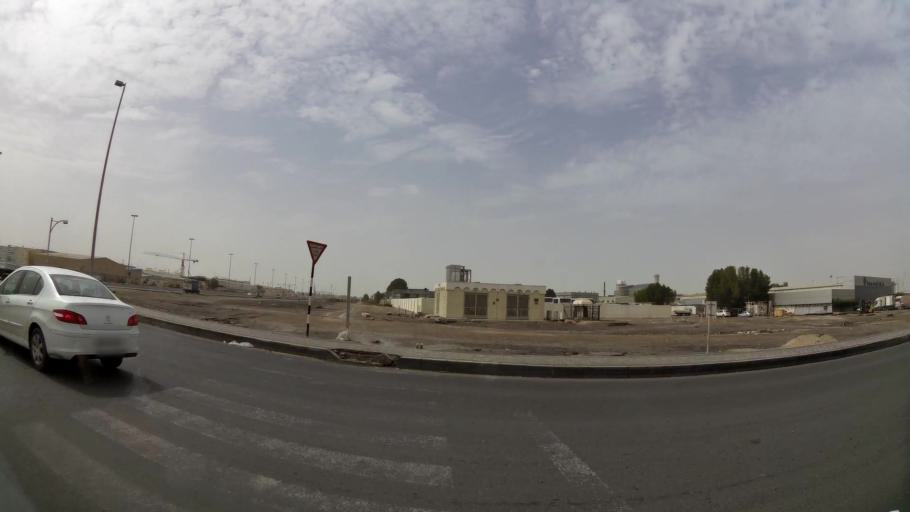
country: AE
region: Abu Dhabi
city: Abu Dhabi
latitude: 24.3452
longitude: 54.4727
